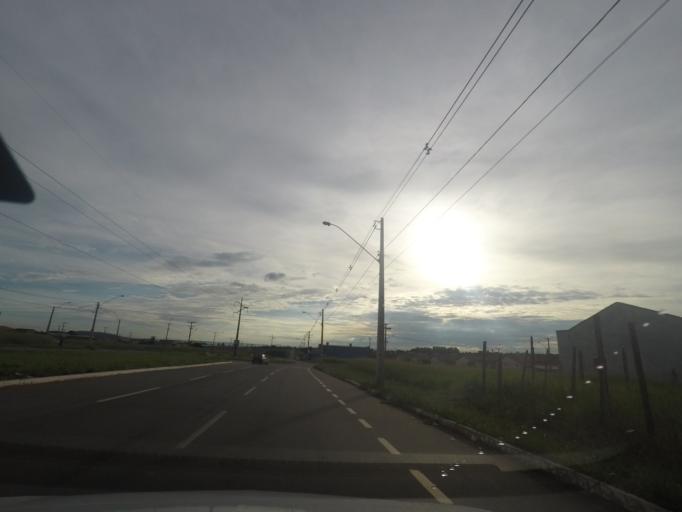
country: BR
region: Goias
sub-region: Trindade
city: Trindade
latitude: -16.7203
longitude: -49.3963
